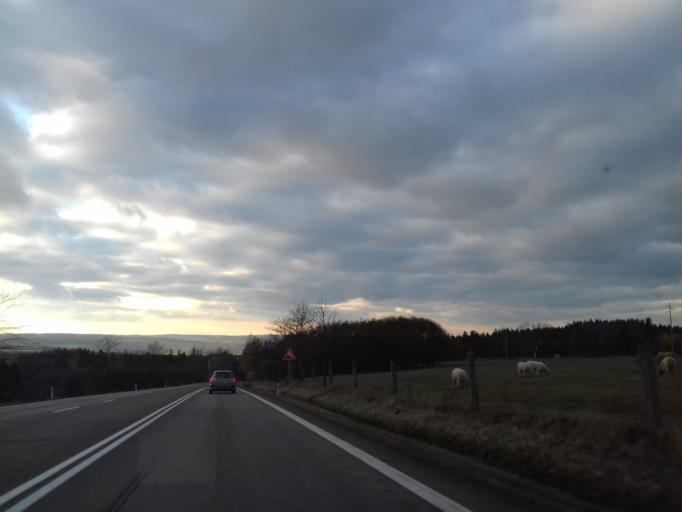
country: CZ
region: Pardubicky
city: Prosec
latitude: 49.7642
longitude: 16.0975
